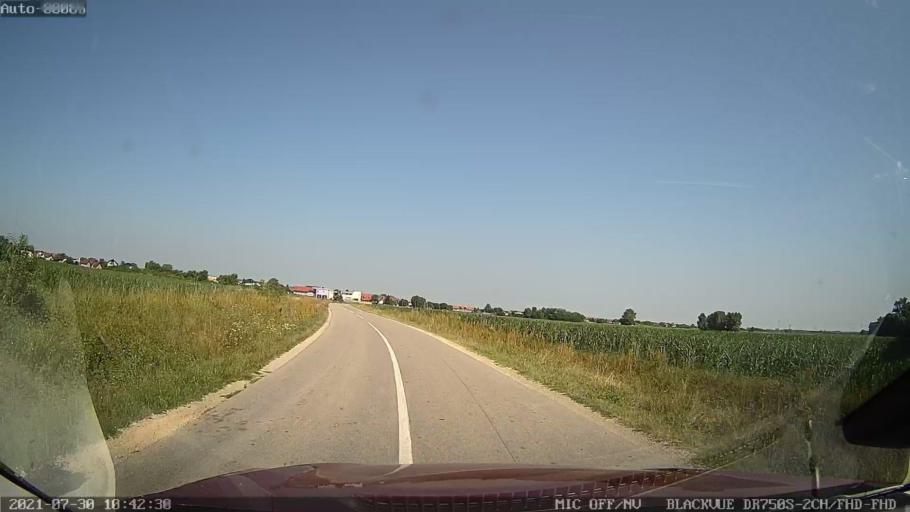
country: HR
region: Medimurska
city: Kursanec
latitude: 46.2853
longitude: 16.4094
